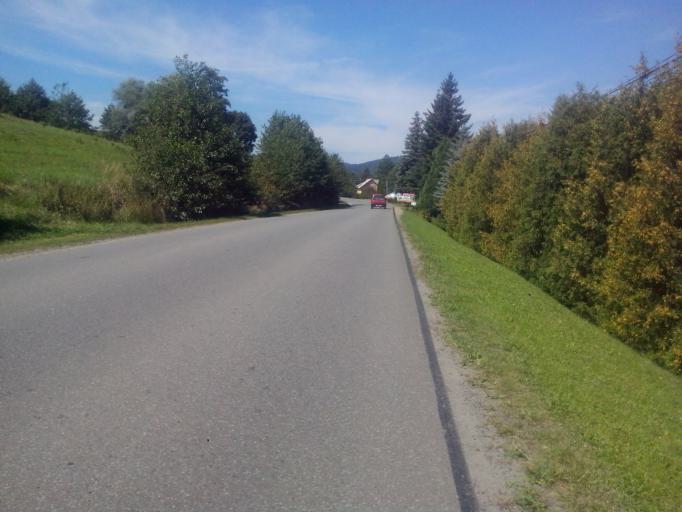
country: PL
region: Subcarpathian Voivodeship
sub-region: Powiat strzyzowski
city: Frysztak
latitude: 49.8670
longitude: 21.6093
